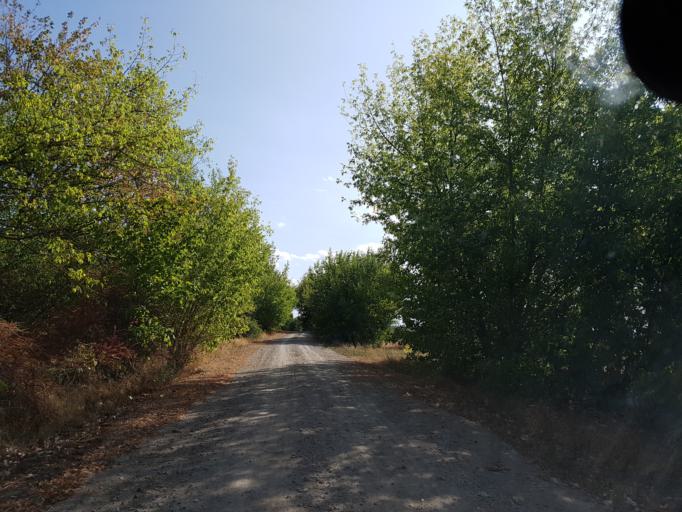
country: DE
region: Brandenburg
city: Treuenbrietzen
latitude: 51.9980
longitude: 12.8571
